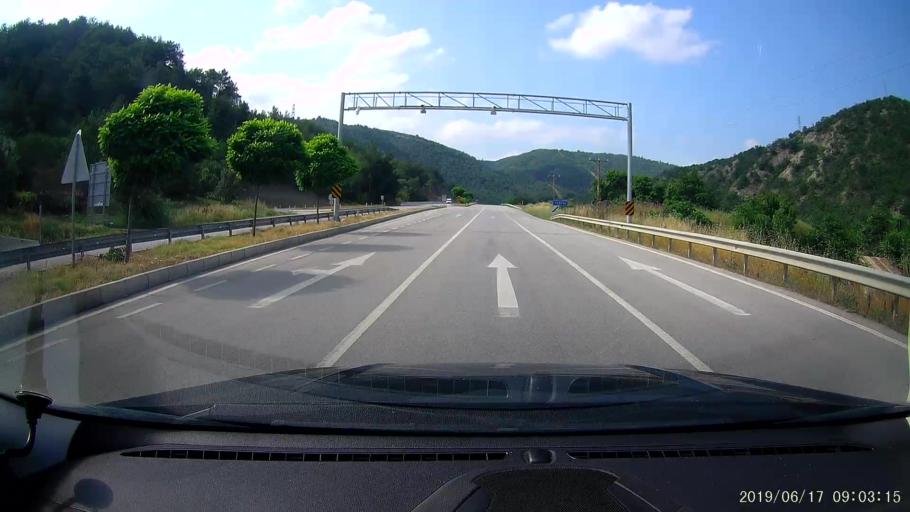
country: TR
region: Amasya
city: Tasova
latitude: 40.7582
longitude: 36.3023
